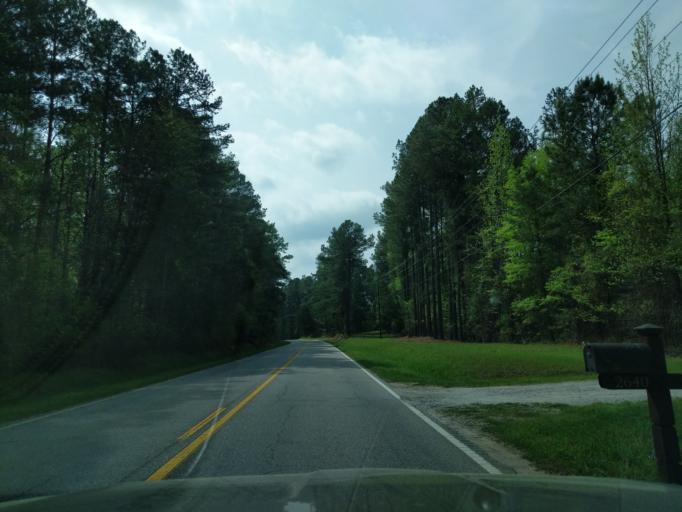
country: US
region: Georgia
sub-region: Columbia County
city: Appling
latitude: 33.5644
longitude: -82.3220
